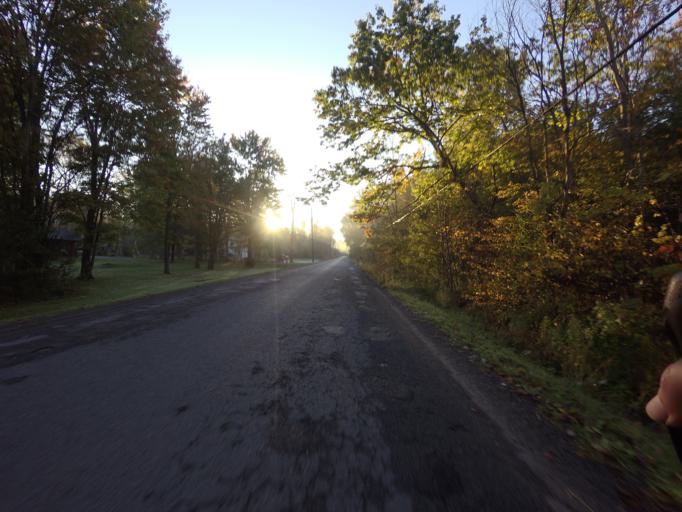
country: CA
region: Ontario
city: Quinte West
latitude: 44.0340
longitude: -77.5814
